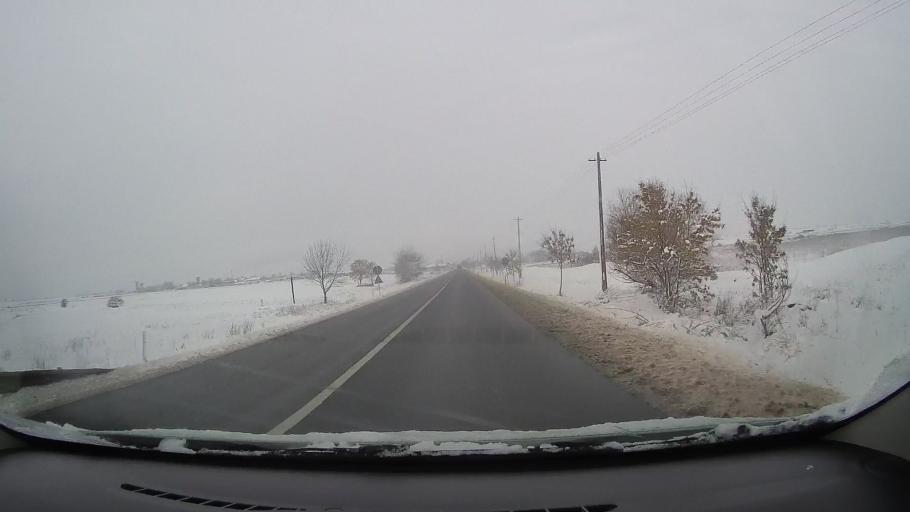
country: RO
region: Alba
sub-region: Municipiul Sebes
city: Lancram
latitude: 45.9853
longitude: 23.5109
